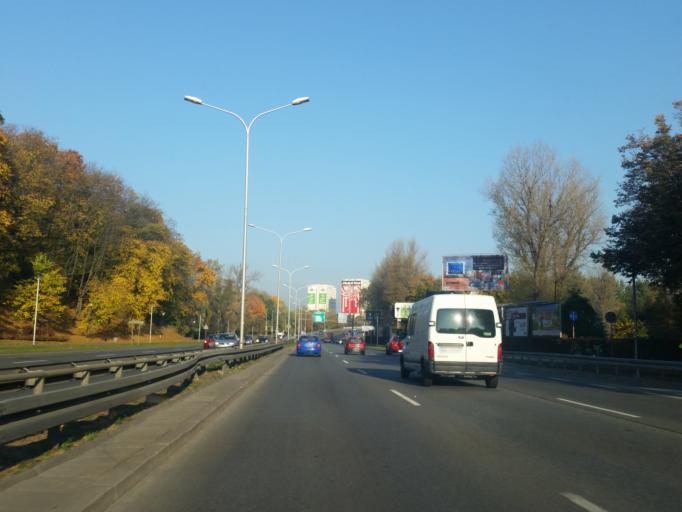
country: PL
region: Masovian Voivodeship
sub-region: Warszawa
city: Zoliborz
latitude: 52.2680
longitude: 21.0013
